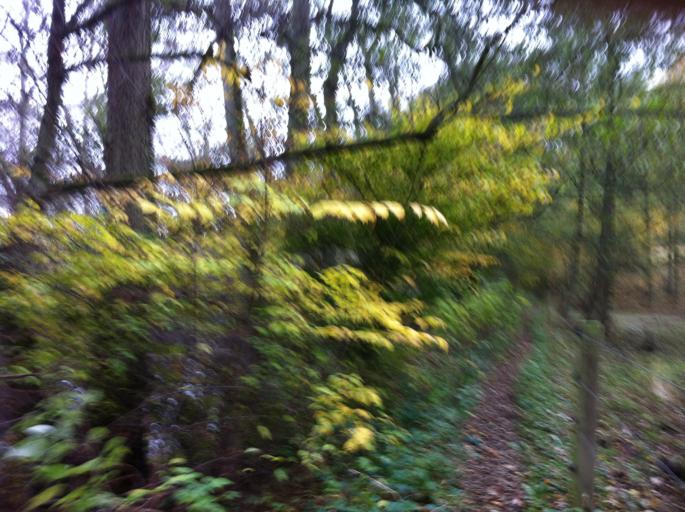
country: SE
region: Skane
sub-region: Helsingborg
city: Gantofta
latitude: 55.9980
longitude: 12.7896
